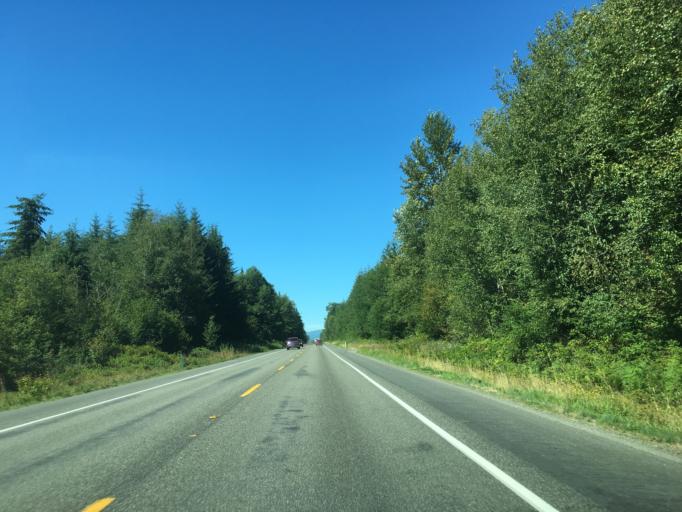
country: US
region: Washington
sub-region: Snohomish County
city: Sisco Heights
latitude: 48.1290
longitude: -122.1127
